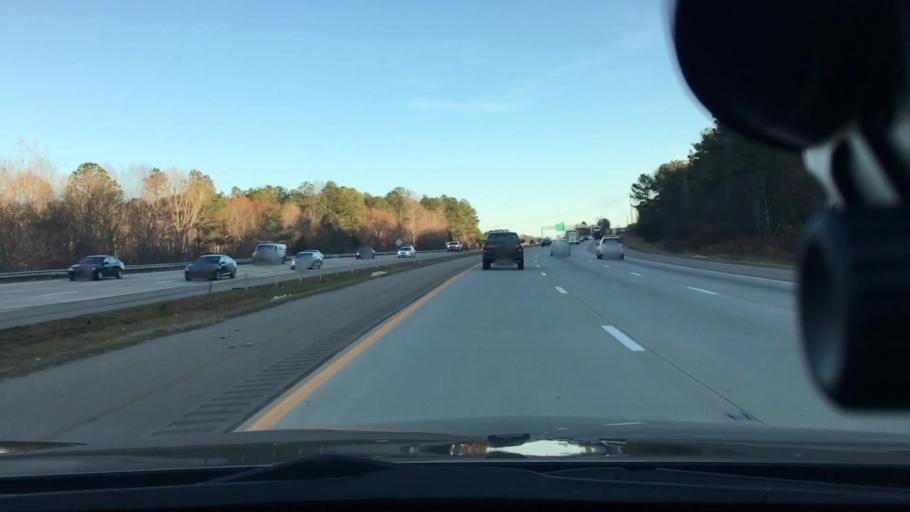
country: US
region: North Carolina
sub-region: Wake County
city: Knightdale
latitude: 35.7714
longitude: -78.5326
